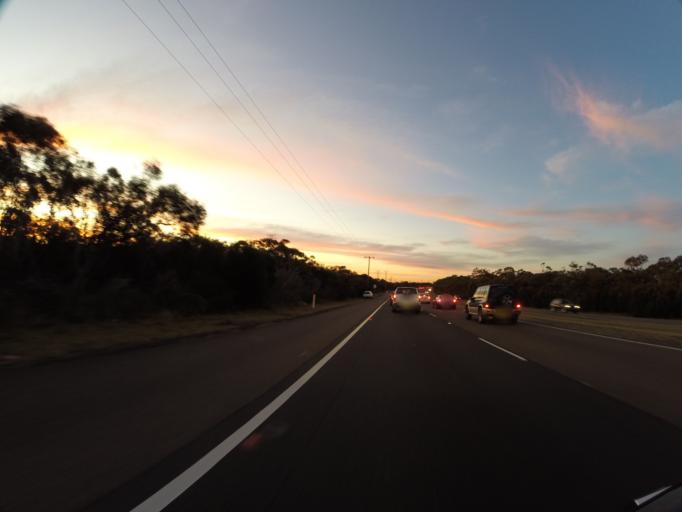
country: AU
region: New South Wales
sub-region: Sutherland Shire
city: Heathcote
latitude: -34.1176
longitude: 150.9916
